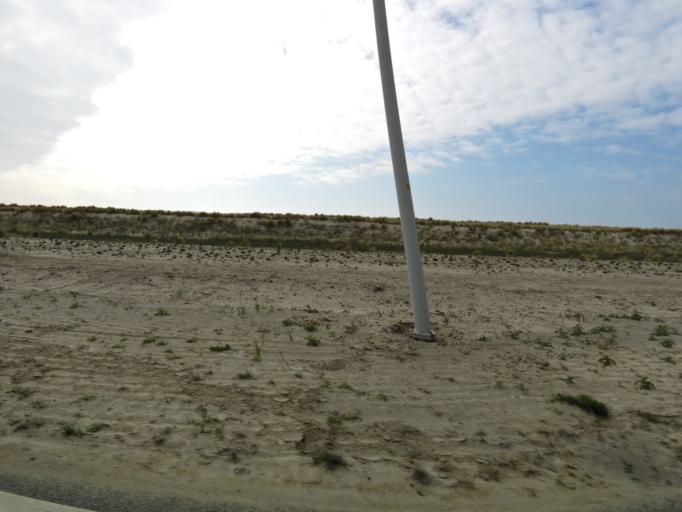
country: NL
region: South Holland
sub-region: Gemeente Goeree-Overflakkee
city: Goedereede
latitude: 51.9618
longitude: 3.9650
